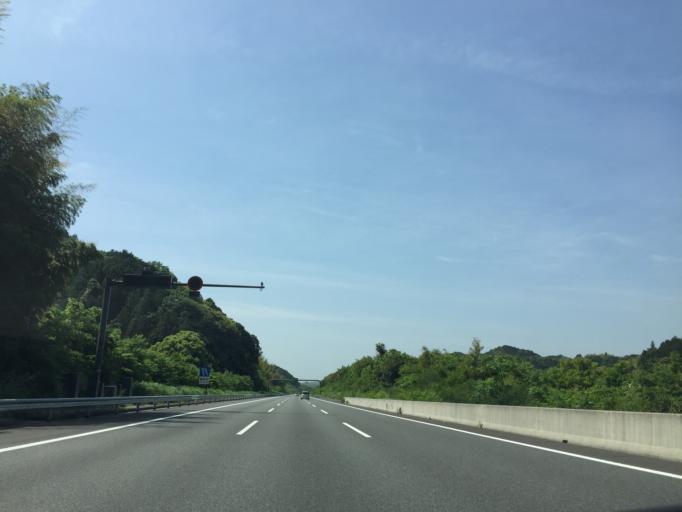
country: JP
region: Shizuoka
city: Fujieda
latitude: 34.9408
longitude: 138.2796
